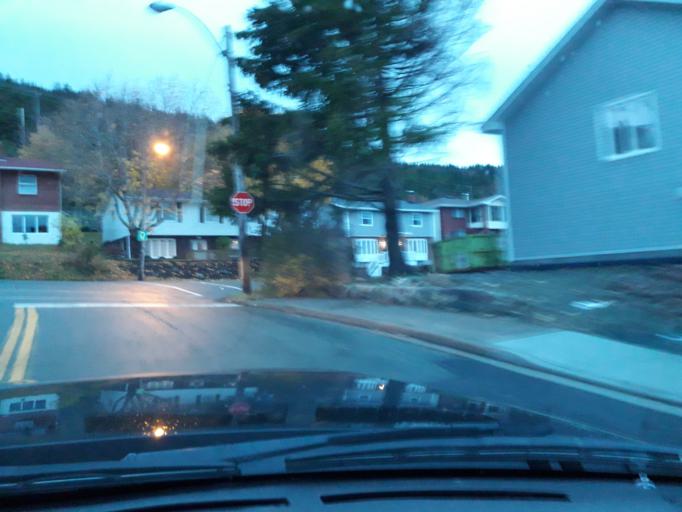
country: CA
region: Newfoundland and Labrador
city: St. John's
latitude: 47.5694
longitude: -52.7482
